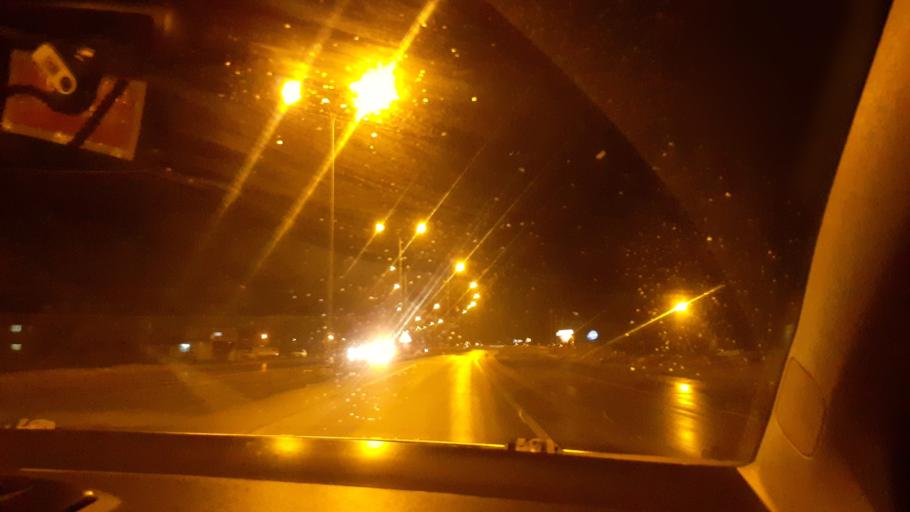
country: TR
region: Hatay
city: Aktepe
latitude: 36.7212
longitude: 36.5156
